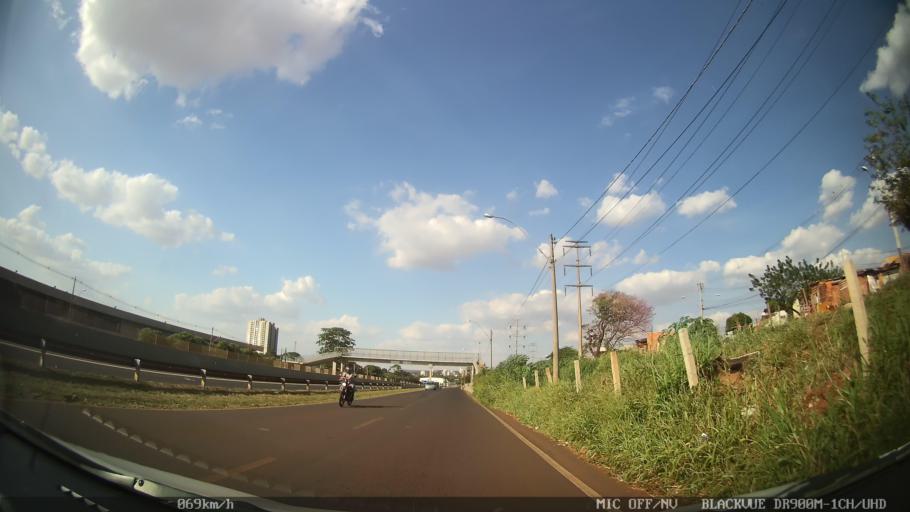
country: BR
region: Sao Paulo
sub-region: Ribeirao Preto
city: Ribeirao Preto
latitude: -21.1788
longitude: -47.8351
